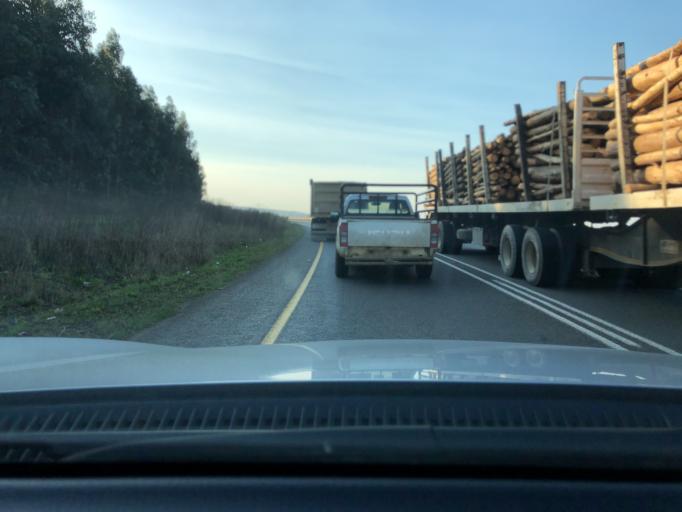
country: ZA
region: KwaZulu-Natal
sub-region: Sisonke District Municipality
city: Ixopo
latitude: -30.2348
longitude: 30.1419
